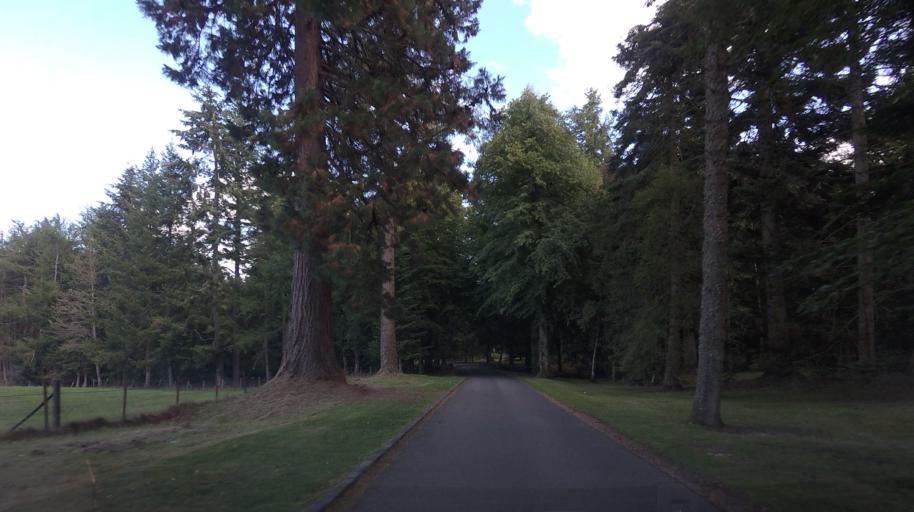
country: GB
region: Scotland
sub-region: Aberdeenshire
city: Banchory
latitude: 57.0596
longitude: -2.4323
